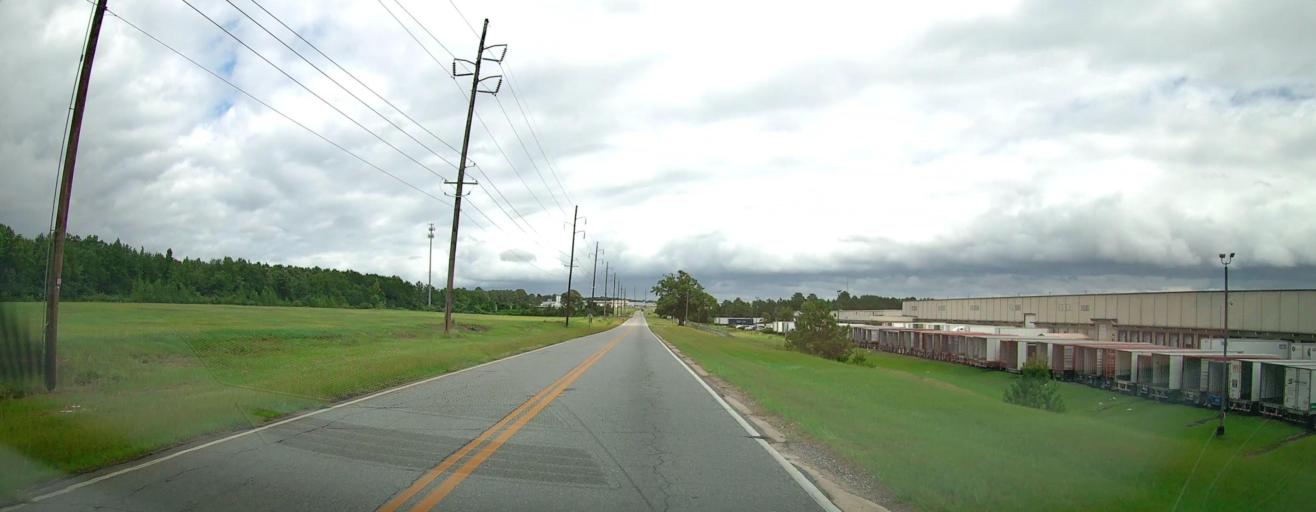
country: US
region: Georgia
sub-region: Bibb County
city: Macon
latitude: 32.7957
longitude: -83.5647
